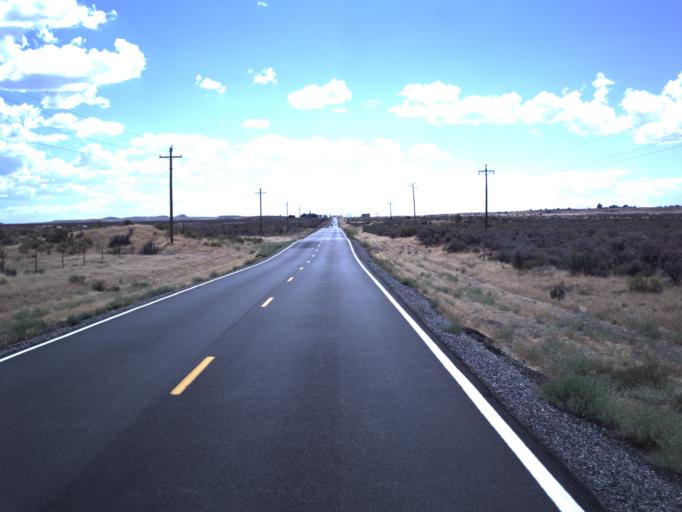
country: US
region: Utah
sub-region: Tooele County
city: Grantsville
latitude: 40.2459
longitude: -112.7083
